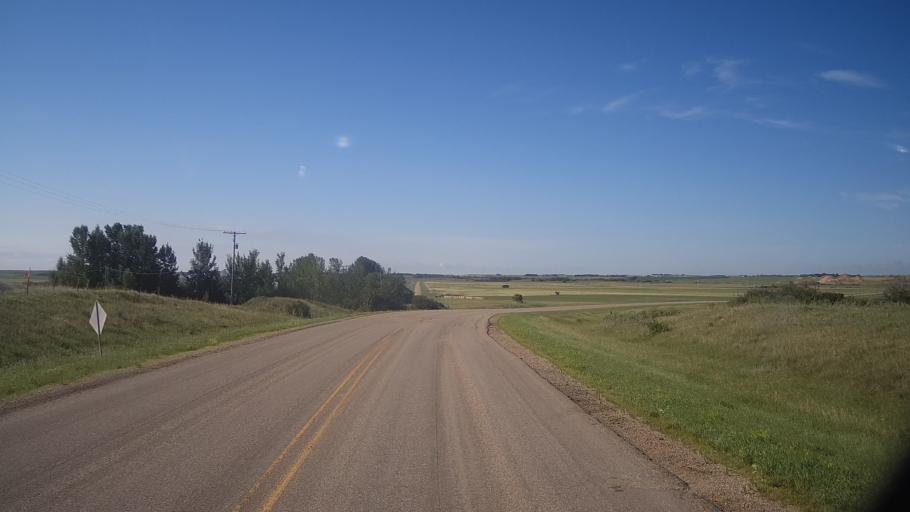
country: CA
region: Saskatchewan
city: Watrous
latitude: 51.7232
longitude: -105.3574
